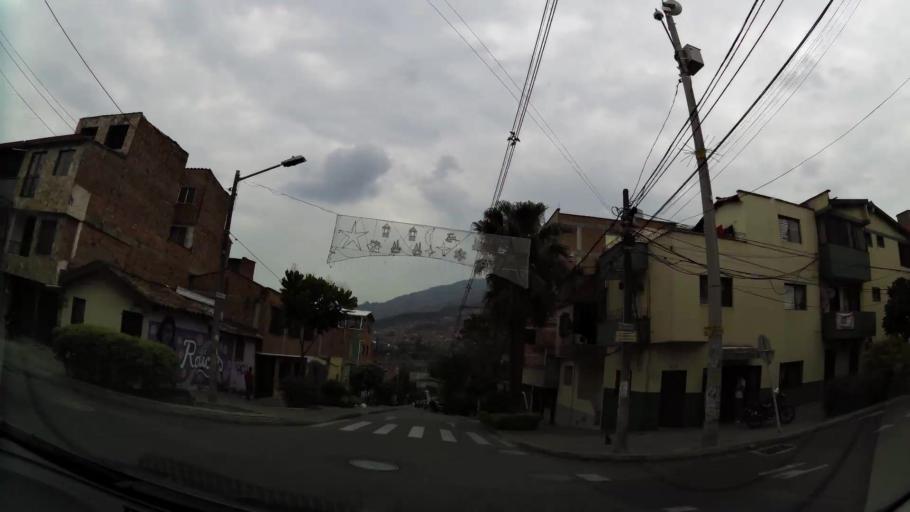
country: CO
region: Antioquia
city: Medellin
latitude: 6.2388
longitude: -75.5529
